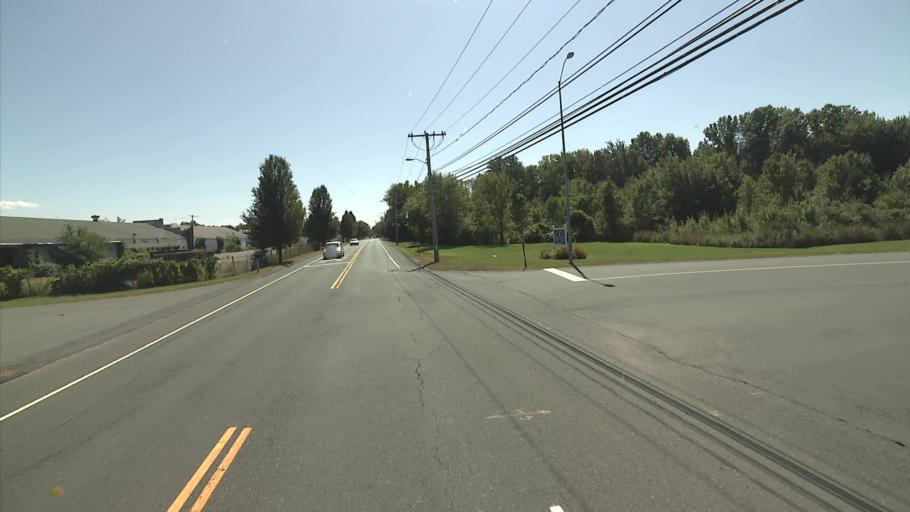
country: US
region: Connecticut
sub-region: Hartford County
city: Windsor Locks
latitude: 41.9480
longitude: -72.6283
